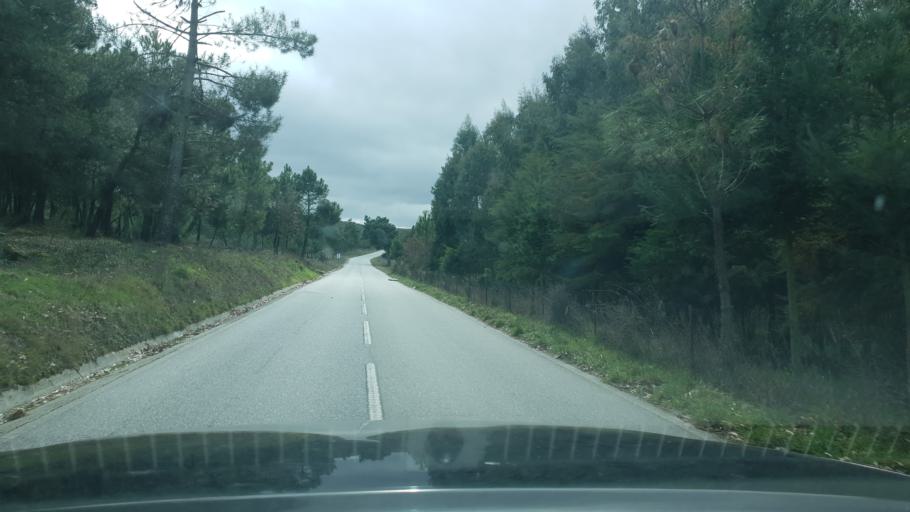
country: PT
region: Viseu
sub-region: Moimenta da Beira
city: Moimenta da Beira
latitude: 41.0373
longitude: -7.5688
